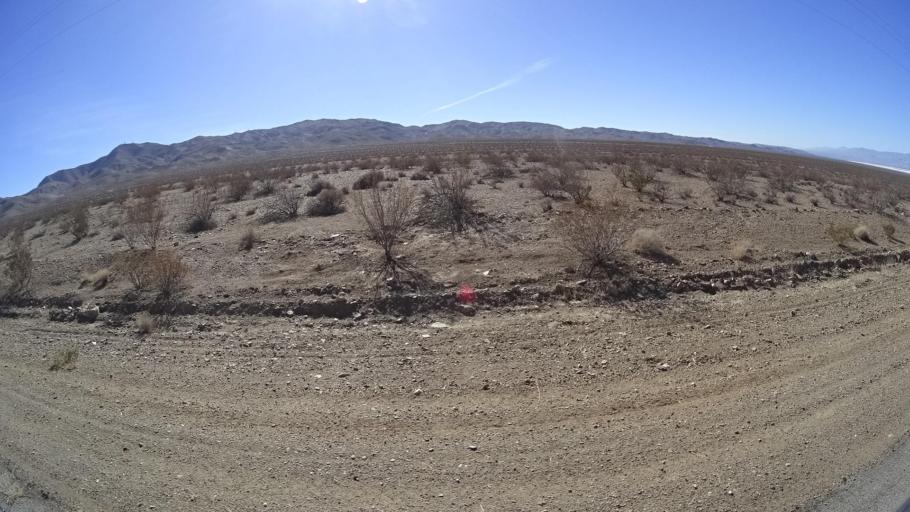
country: US
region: California
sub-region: Kern County
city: Ridgecrest
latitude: 35.3831
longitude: -117.7013
